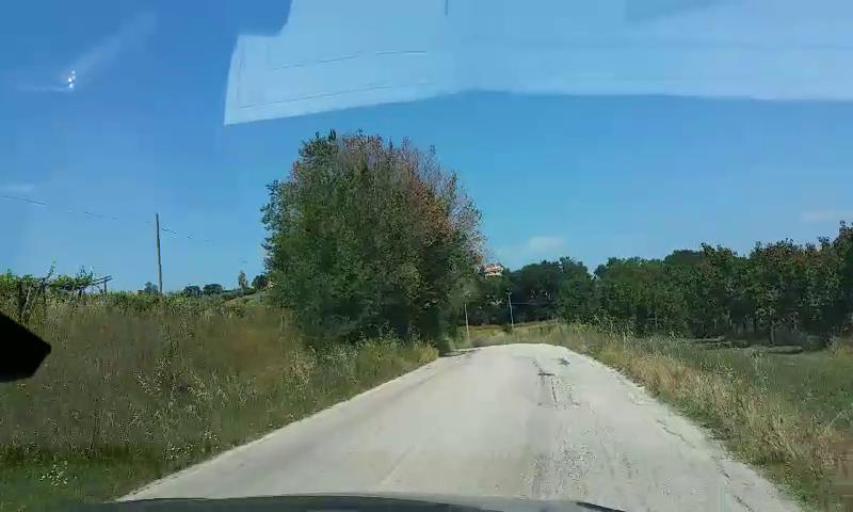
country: IT
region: Molise
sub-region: Provincia di Campobasso
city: San Giacomo degli Schiavoni
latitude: 41.9714
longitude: 14.9024
